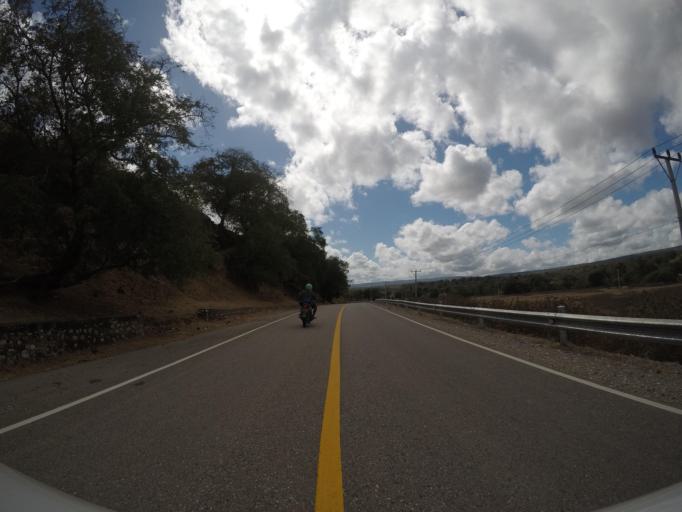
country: TL
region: Lautem
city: Lospalos
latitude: -8.4030
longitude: 126.8286
